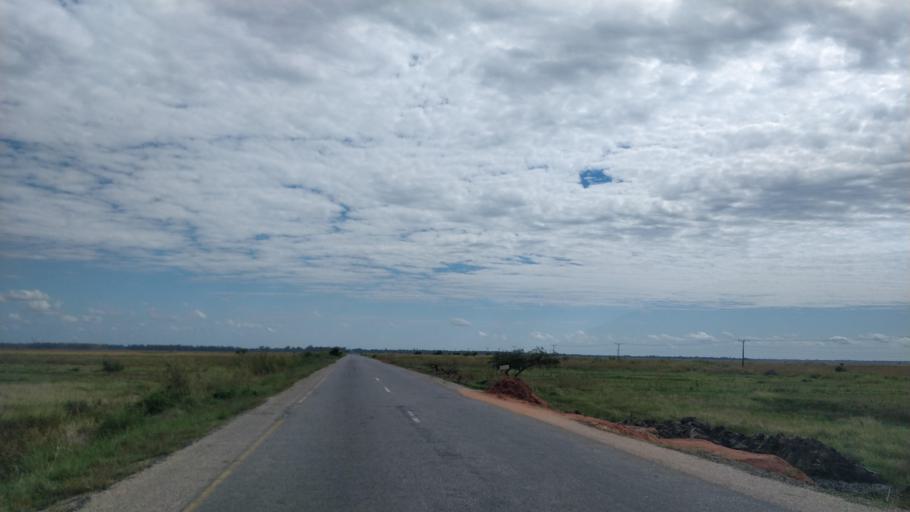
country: MZ
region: Zambezia
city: Quelimane
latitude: -17.6539
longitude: 36.8545
